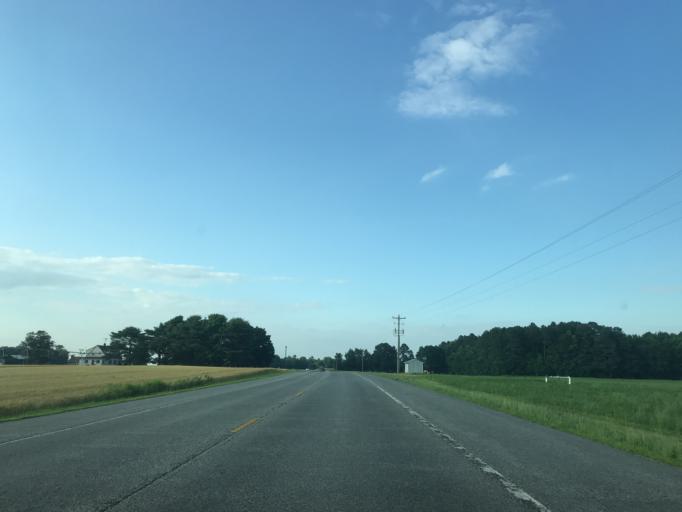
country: US
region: Maryland
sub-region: Caroline County
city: Denton
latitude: 38.8179
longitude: -75.7805
